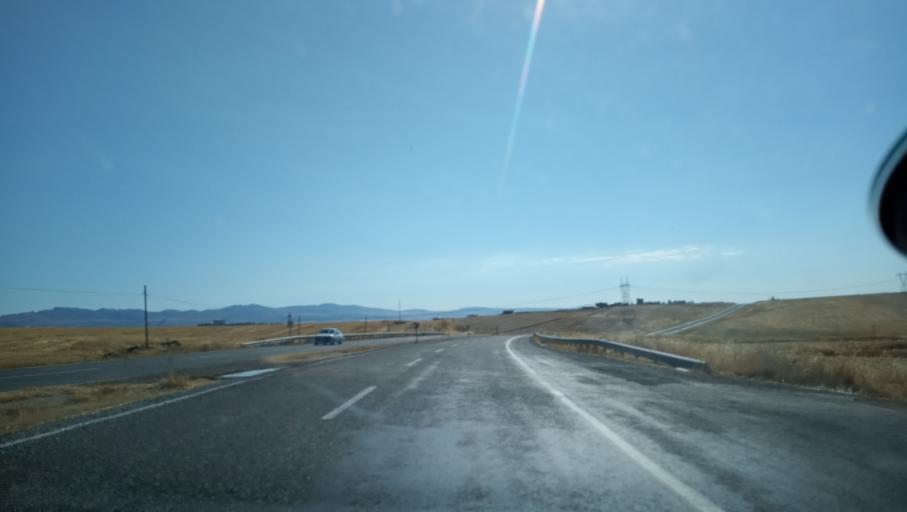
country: TR
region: Diyarbakir
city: Bagdere
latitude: 38.1307
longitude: 40.7617
